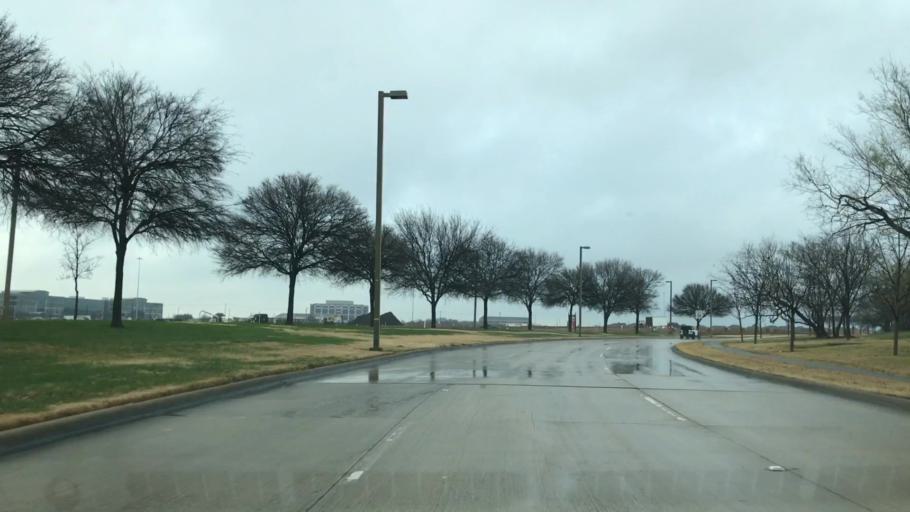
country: US
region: Texas
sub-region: Dallas County
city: Farmers Branch
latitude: 32.9009
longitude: -96.9536
